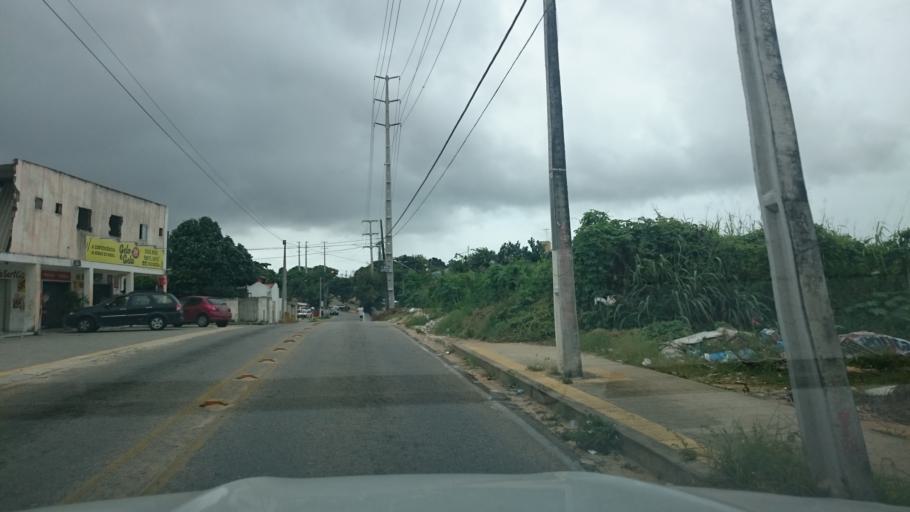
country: BR
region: Rio Grande do Norte
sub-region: Parnamirim
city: Parnamirim
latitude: -5.8769
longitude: -35.2100
